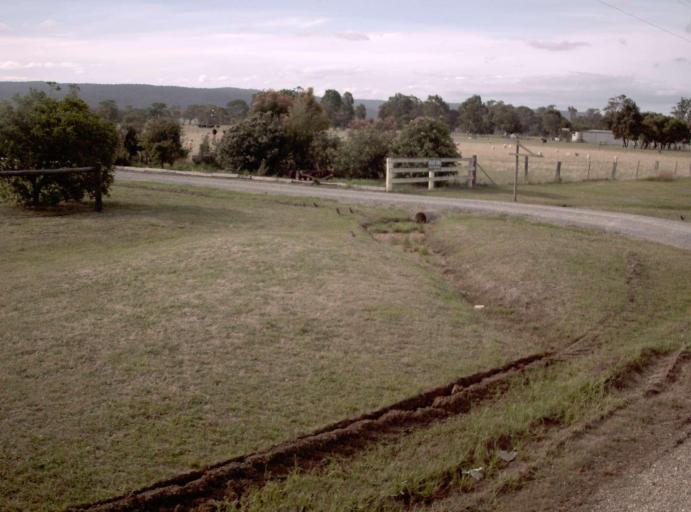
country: AU
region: Victoria
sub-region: Wellington
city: Heyfield
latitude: -38.0351
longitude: 146.6670
